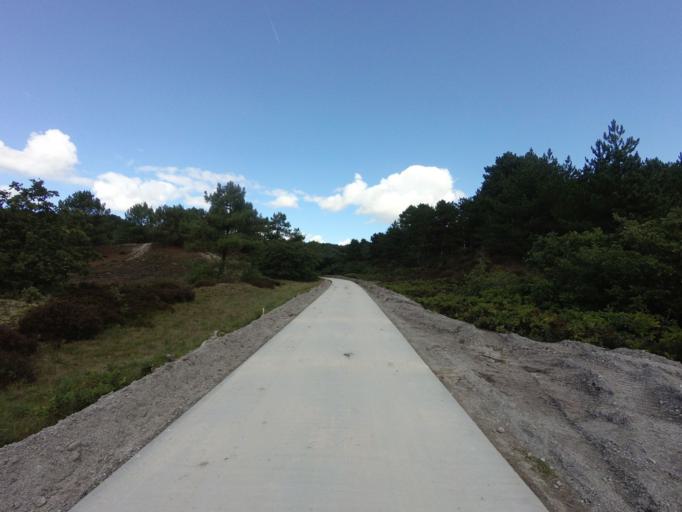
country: NL
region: North Holland
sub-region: Gemeente Bergen
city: Egmond aan Zee
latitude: 52.7170
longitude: 4.6630
